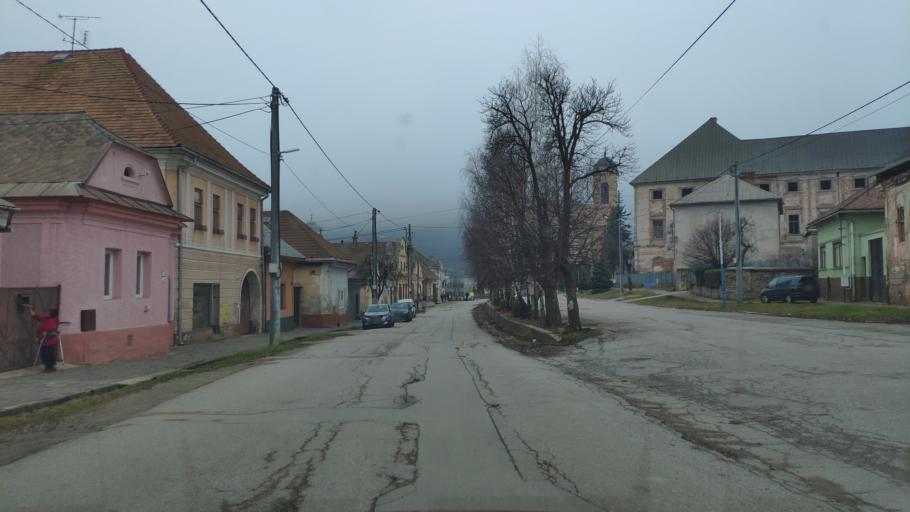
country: SK
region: Banskobystricky
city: Revuca
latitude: 48.6324
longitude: 20.2366
